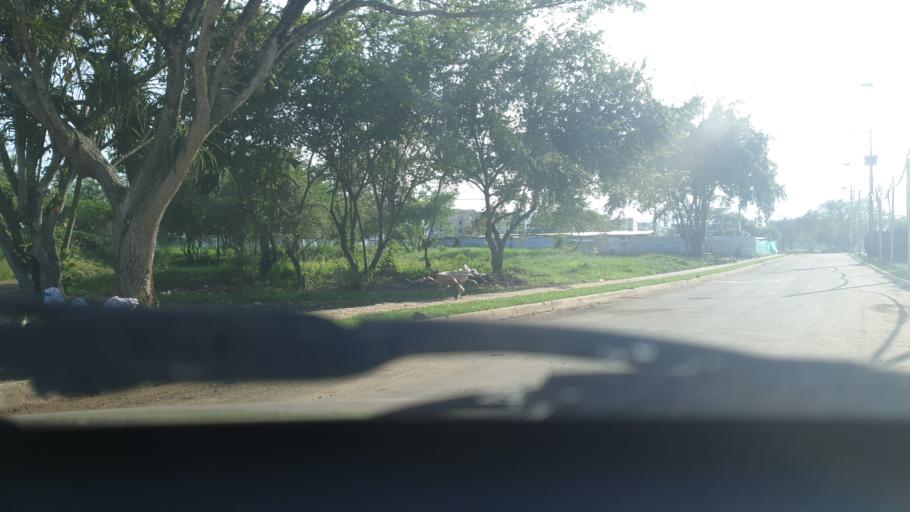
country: CO
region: Valle del Cauca
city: Jamundi
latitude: 3.3469
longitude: -76.5137
